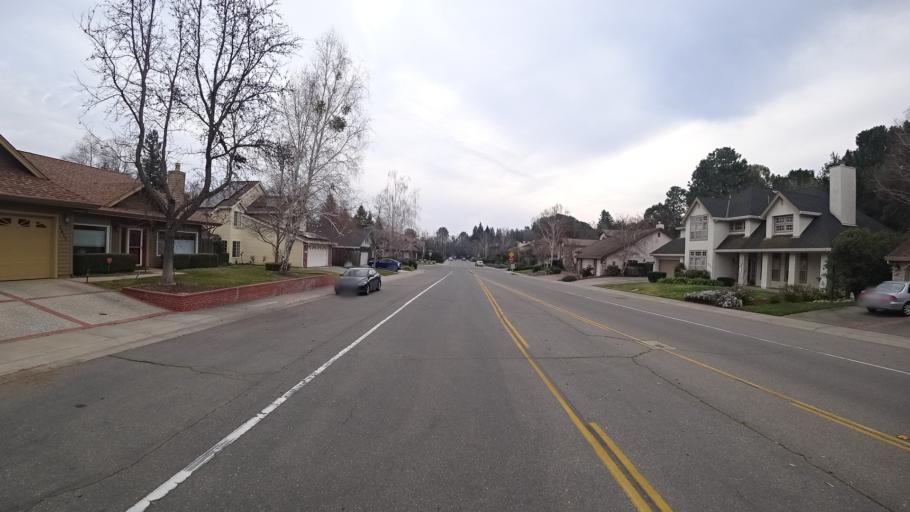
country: US
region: California
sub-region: Yolo County
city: Davis
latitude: 38.5431
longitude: -121.7078
